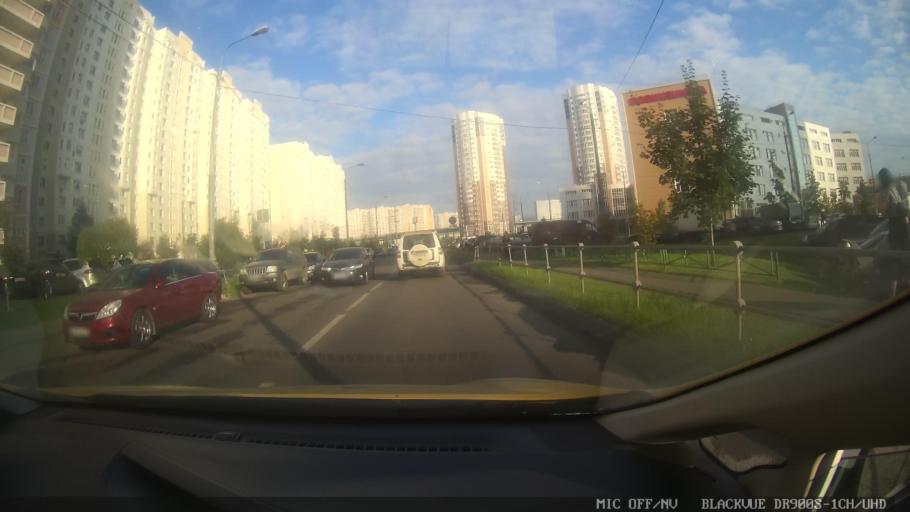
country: RU
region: Moscow
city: Nekrasovka
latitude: 55.6929
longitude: 37.9160
